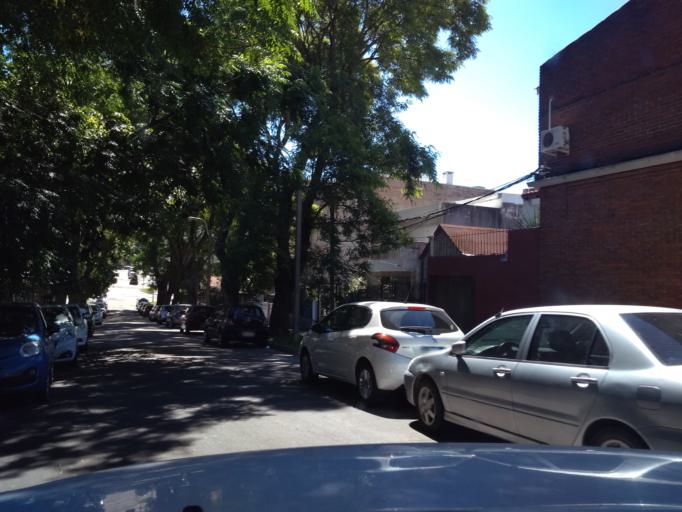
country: UY
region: Montevideo
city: Montevideo
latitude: -34.9011
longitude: -56.1325
